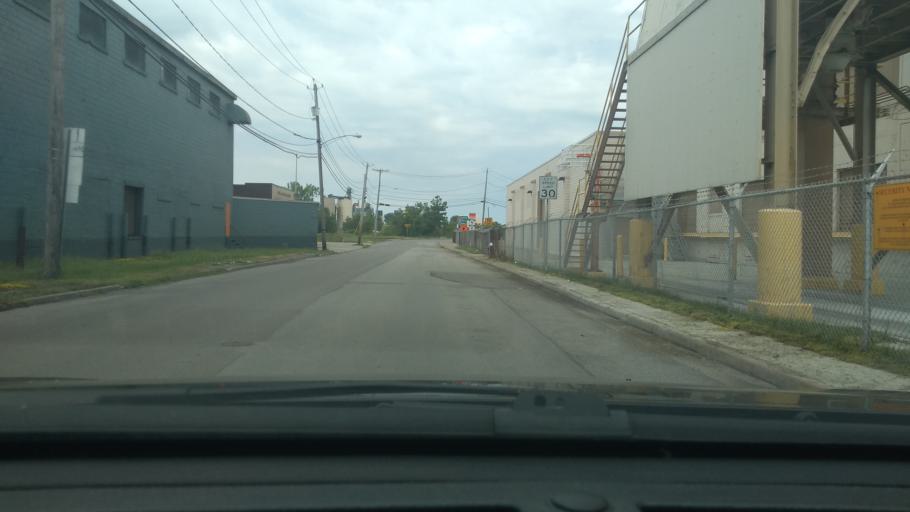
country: US
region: New York
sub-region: Erie County
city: Buffalo
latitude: 42.8609
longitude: -78.8680
